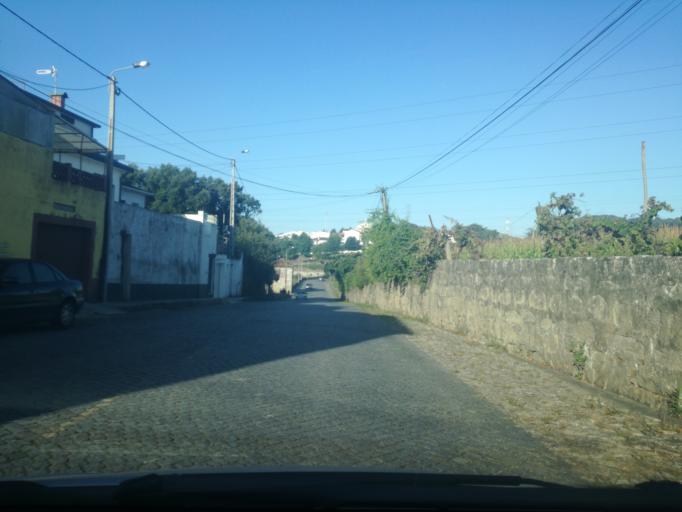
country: PT
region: Porto
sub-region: Maia
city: Leca do Bailio
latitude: 41.2082
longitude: -8.6183
